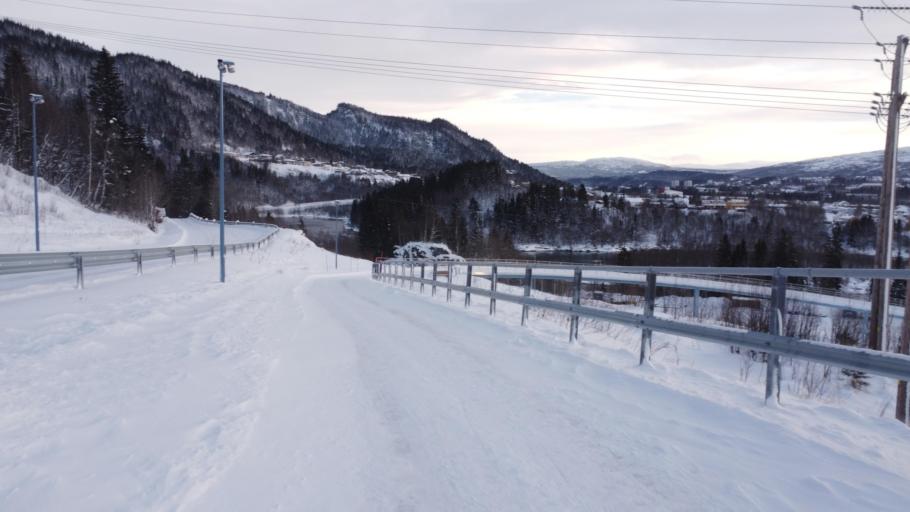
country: NO
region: Nordland
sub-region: Rana
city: Mo i Rana
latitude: 66.3300
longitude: 14.1603
